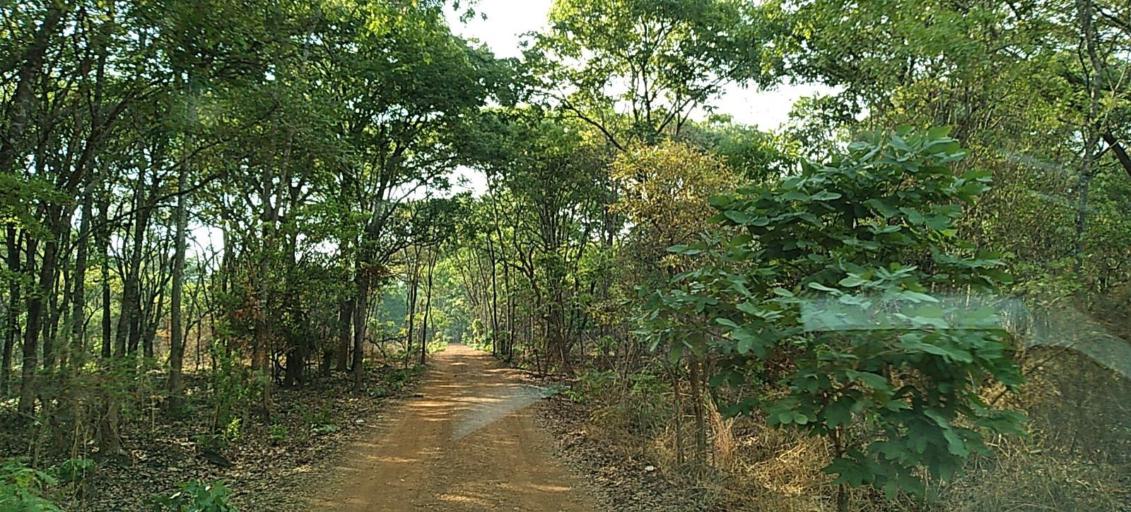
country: ZM
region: Copperbelt
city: Kalulushi
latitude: -12.9996
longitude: 27.7099
